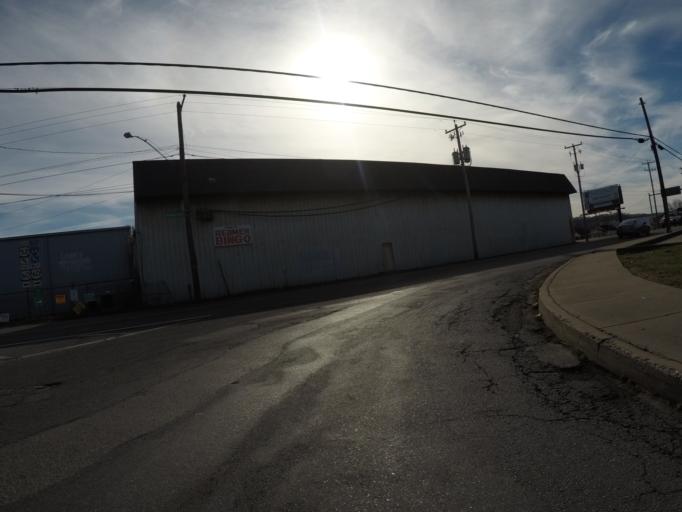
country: US
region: West Virginia
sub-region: Cabell County
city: Huntington
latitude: 38.4104
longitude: -82.4862
